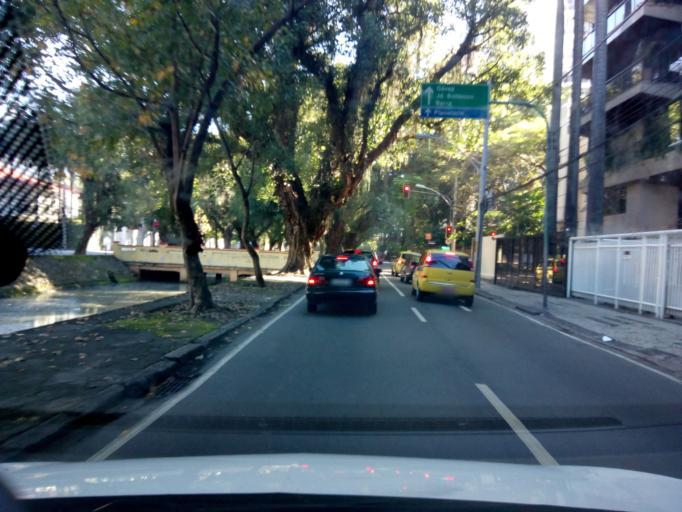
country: BR
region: Rio de Janeiro
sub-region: Rio De Janeiro
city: Rio de Janeiro
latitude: -22.9837
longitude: -43.2284
